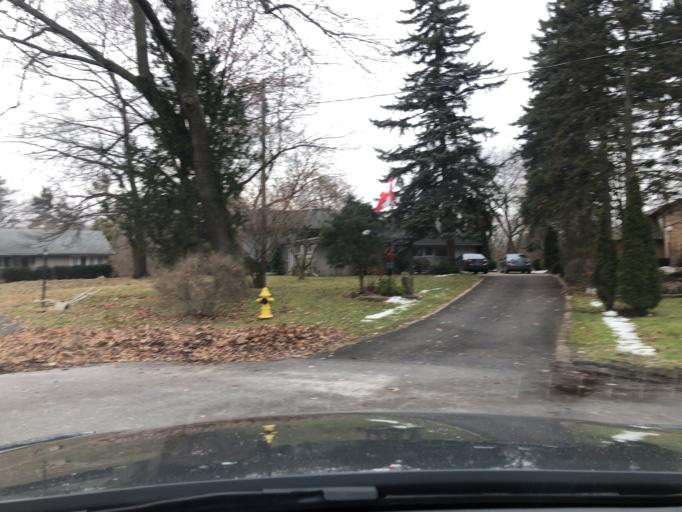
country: CA
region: Ontario
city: Etobicoke
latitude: 43.6934
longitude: -79.5277
